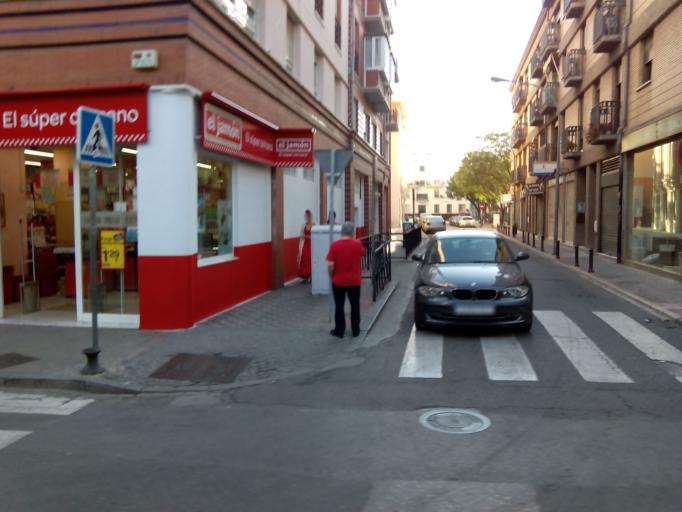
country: ES
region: Andalusia
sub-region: Provincia de Sevilla
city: Camas
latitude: 37.3839
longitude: -6.0060
